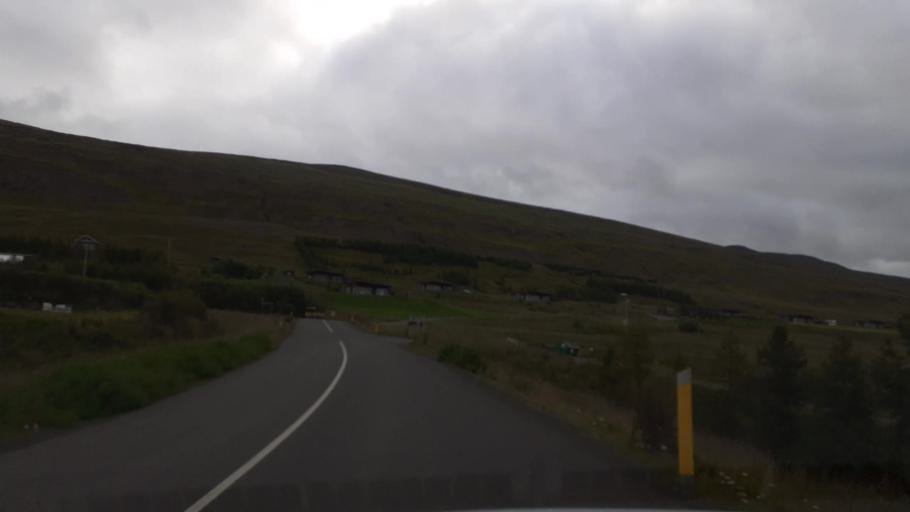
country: IS
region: Northeast
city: Akureyri
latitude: 65.6794
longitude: -18.0388
